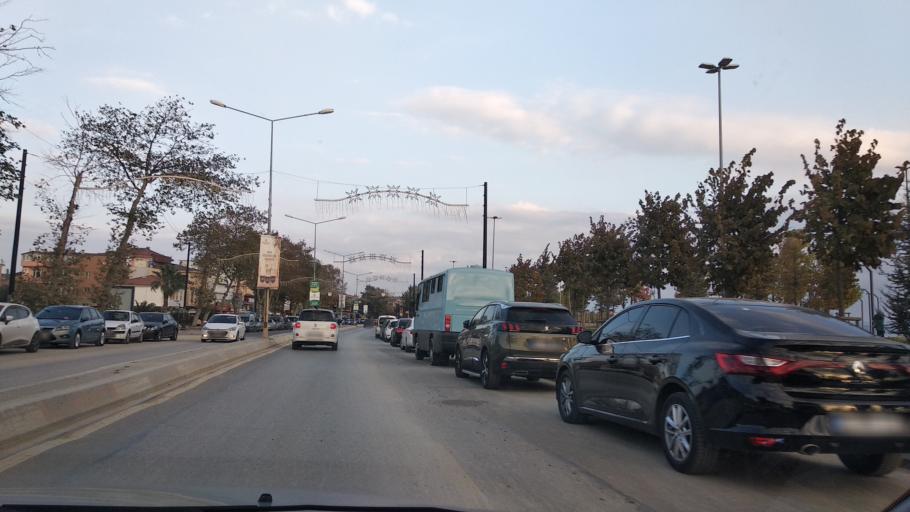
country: TR
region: Istanbul
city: Icmeler
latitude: 40.8165
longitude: 29.2992
